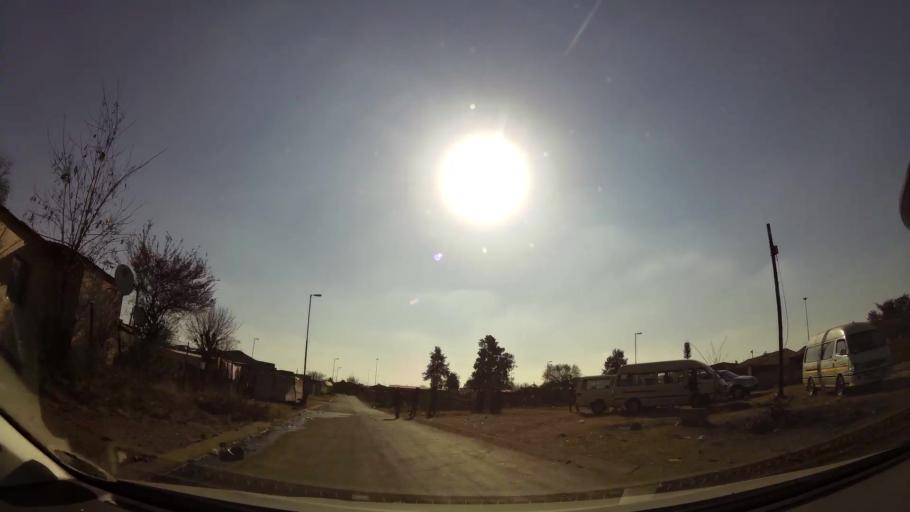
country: ZA
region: Gauteng
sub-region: City of Johannesburg Metropolitan Municipality
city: Soweto
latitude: -26.2799
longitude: 27.8756
